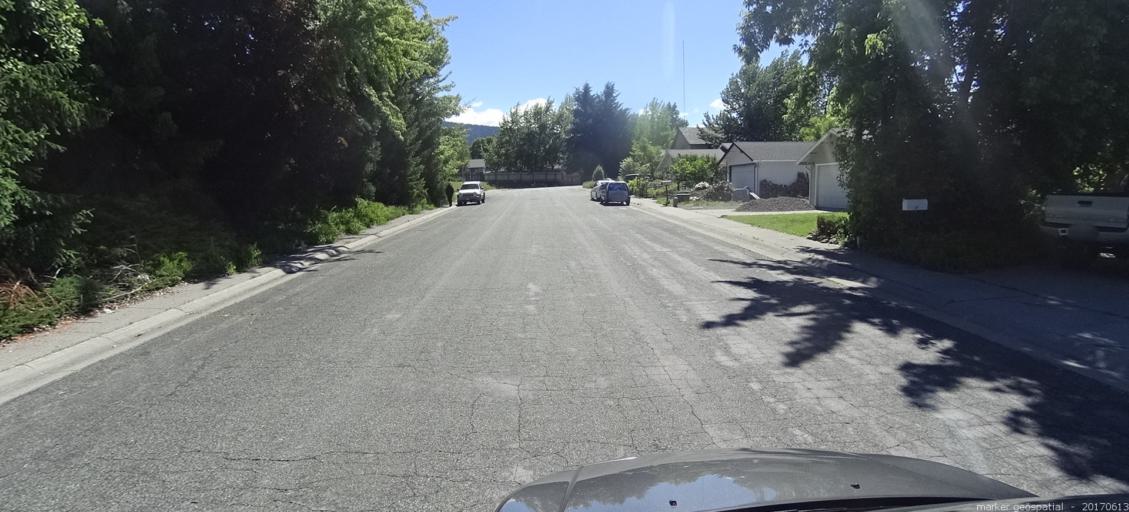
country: US
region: California
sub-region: Siskiyou County
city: Mount Shasta
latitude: 41.3201
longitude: -122.3148
